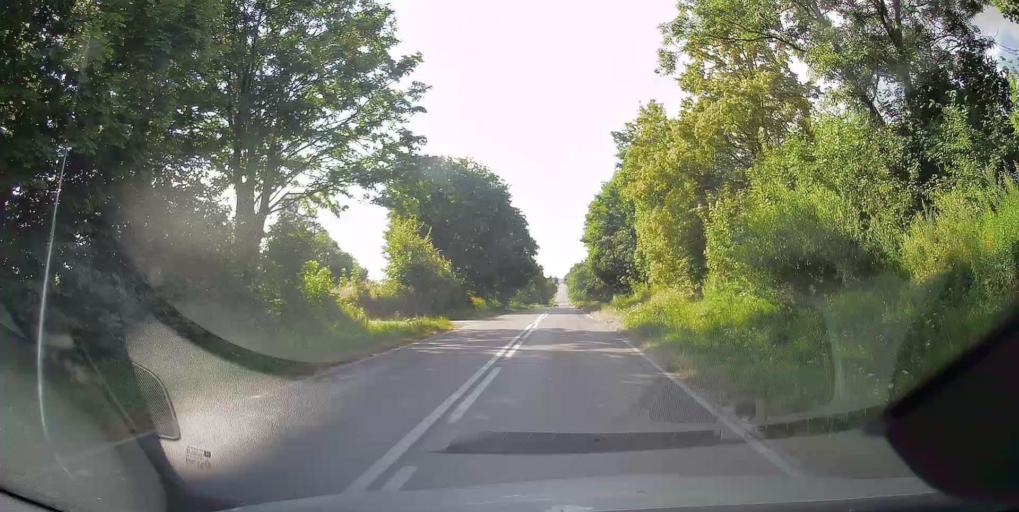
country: PL
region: Swietokrzyskie
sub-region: Powiat kielecki
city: Bodzentyn
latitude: 50.9670
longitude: 20.8901
